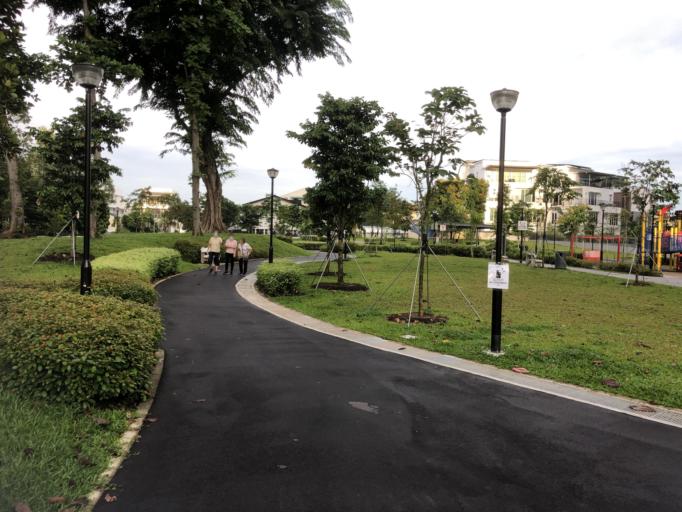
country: MY
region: Johor
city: Kampung Pasir Gudang Baru
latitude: 1.3974
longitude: 103.8751
